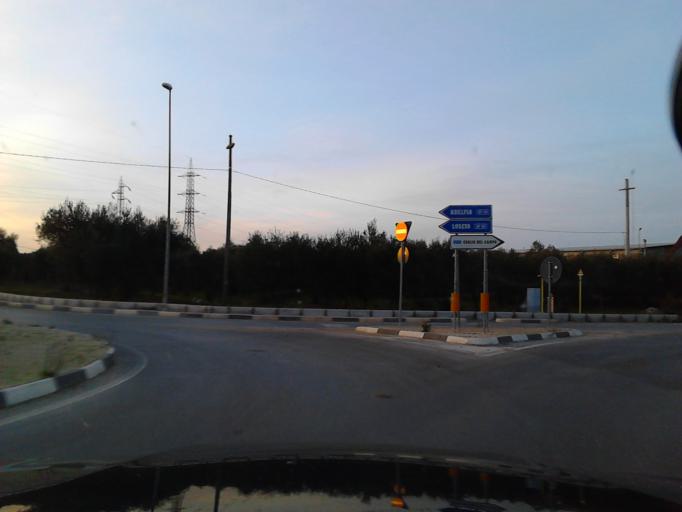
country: IT
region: Apulia
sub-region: Provincia di Bari
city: Lamie
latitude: 41.0398
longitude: 16.8633
